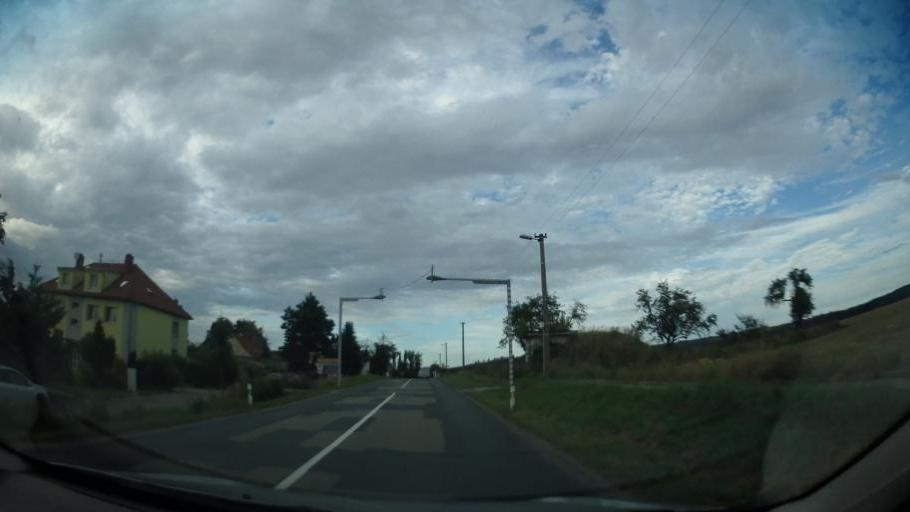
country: CZ
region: South Moravian
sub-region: Okres Blansko
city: Boskovice
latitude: 49.4975
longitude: 16.6646
